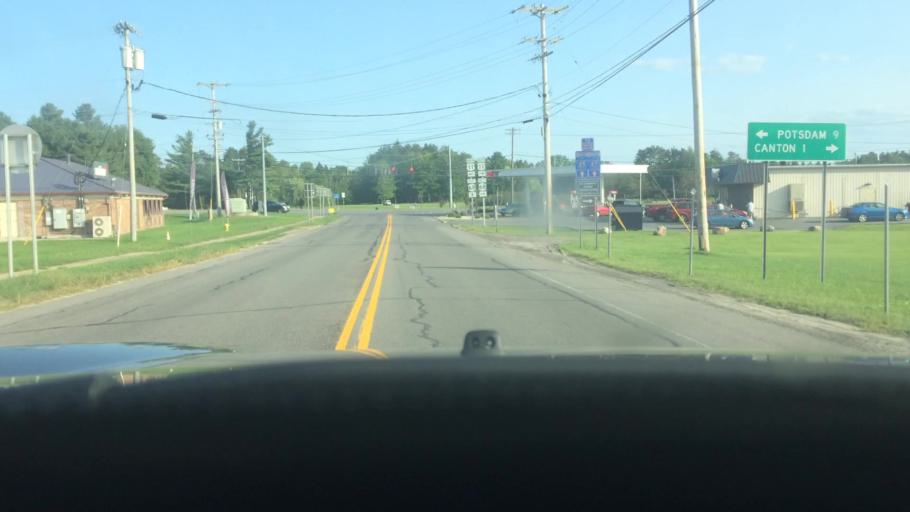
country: US
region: New York
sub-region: St. Lawrence County
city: Canton
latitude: 44.5983
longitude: -75.1482
